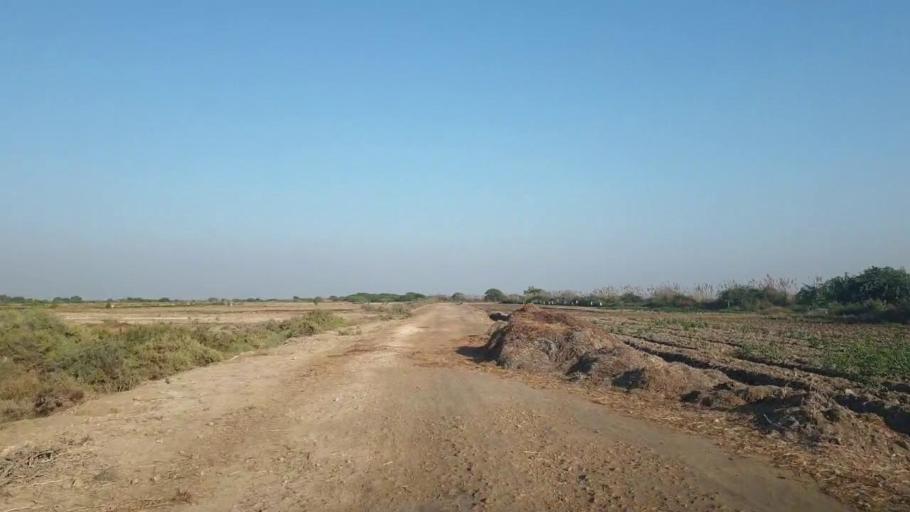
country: PK
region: Sindh
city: Mirpur Sakro
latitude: 24.5352
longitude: 67.5321
